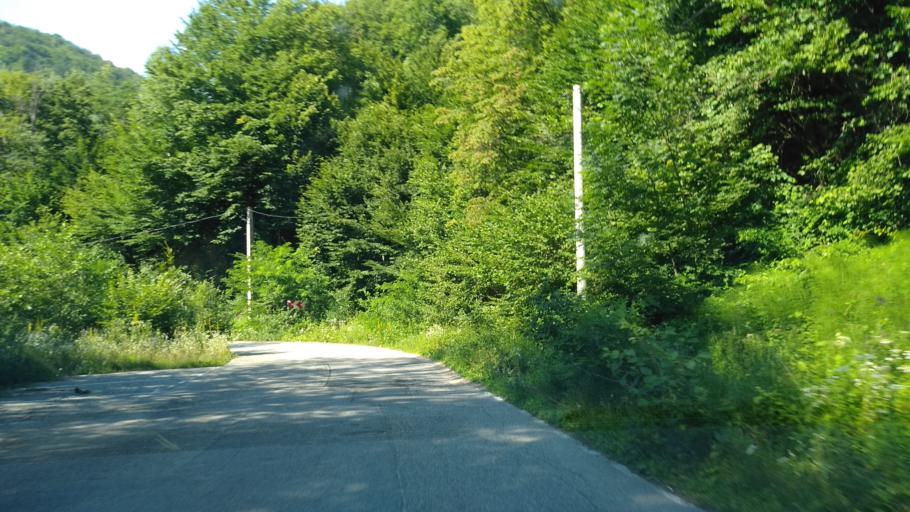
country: RO
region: Hunedoara
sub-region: Comuna Orastioara de Sus
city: Orastioara de Sus
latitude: 45.6599
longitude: 23.1813
